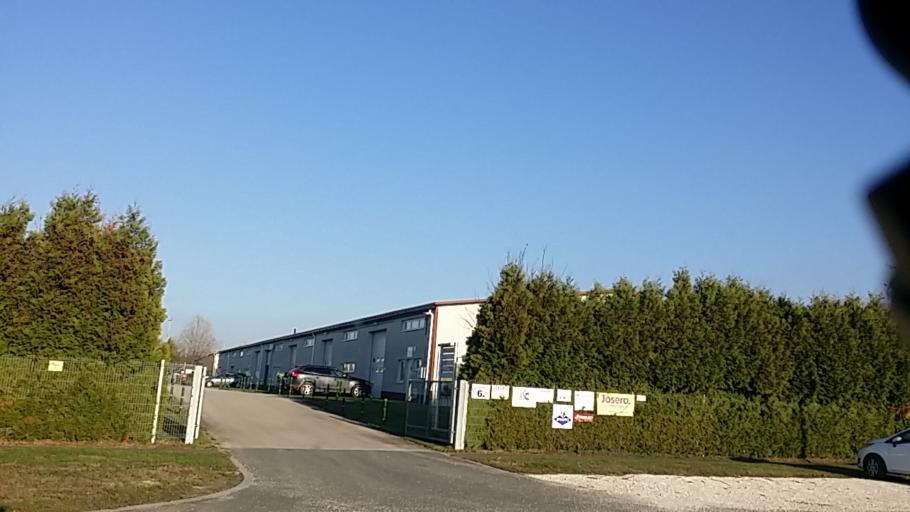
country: HU
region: Budapest
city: Budapest XVII. keruelet
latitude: 47.4939
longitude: 19.2299
